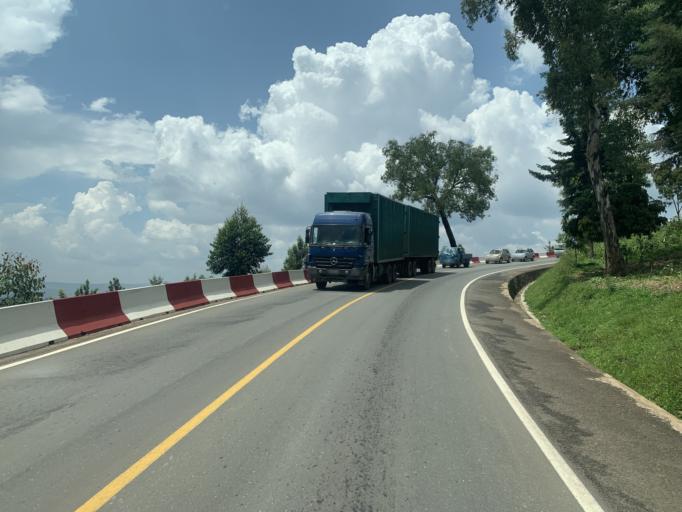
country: RW
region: Southern Province
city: Gitarama
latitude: -2.0019
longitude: 29.8979
